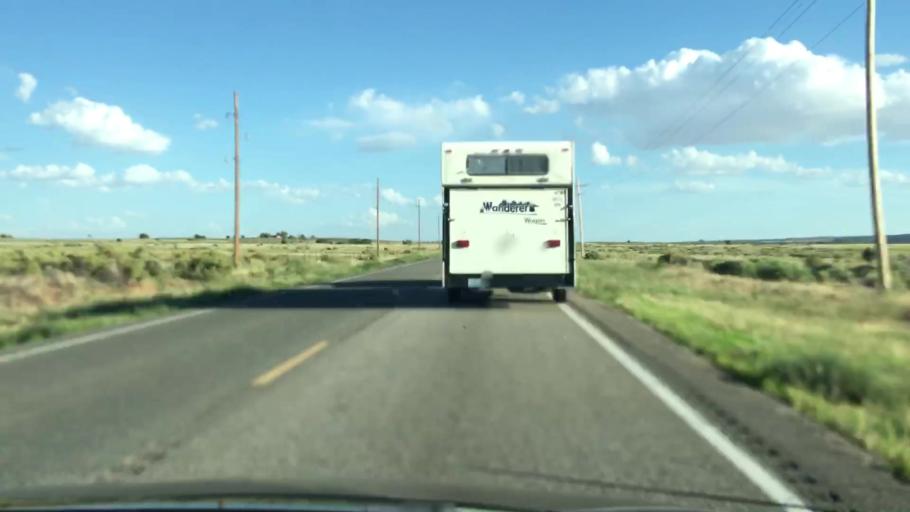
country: US
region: Arizona
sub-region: Mohave County
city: Colorado City
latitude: 37.0692
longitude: -113.1037
